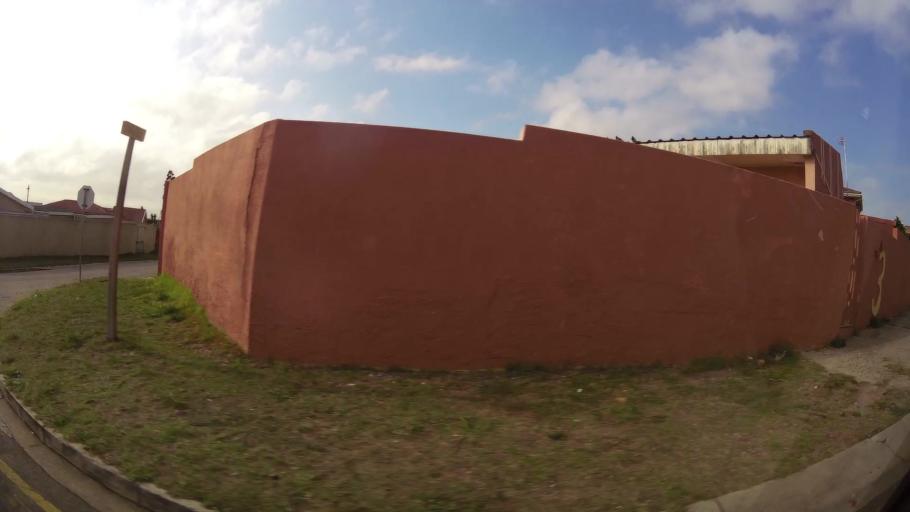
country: ZA
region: Eastern Cape
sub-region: Nelson Mandela Bay Metropolitan Municipality
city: Port Elizabeth
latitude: -33.9240
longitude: 25.5526
